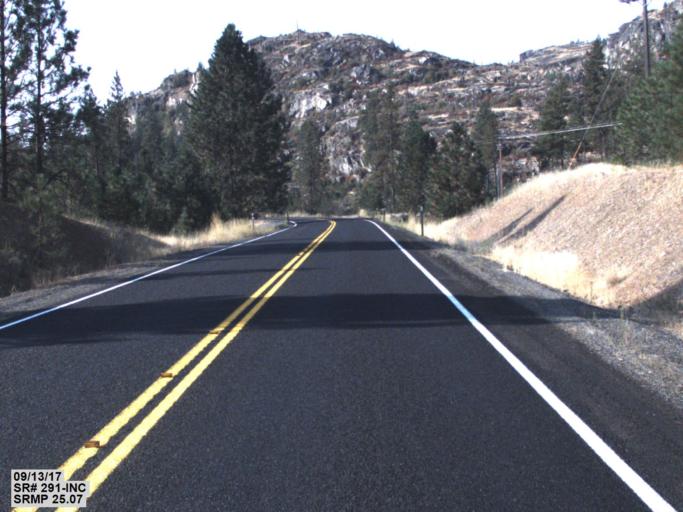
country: US
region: Washington
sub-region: Spokane County
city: Airway Heights
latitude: 47.8647
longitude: -117.7107
